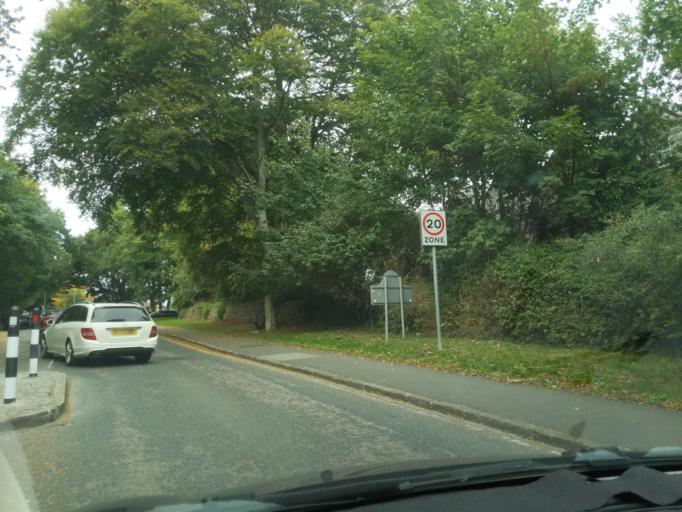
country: GB
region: England
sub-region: Cornwall
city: St Austell
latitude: 50.3368
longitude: -4.7643
